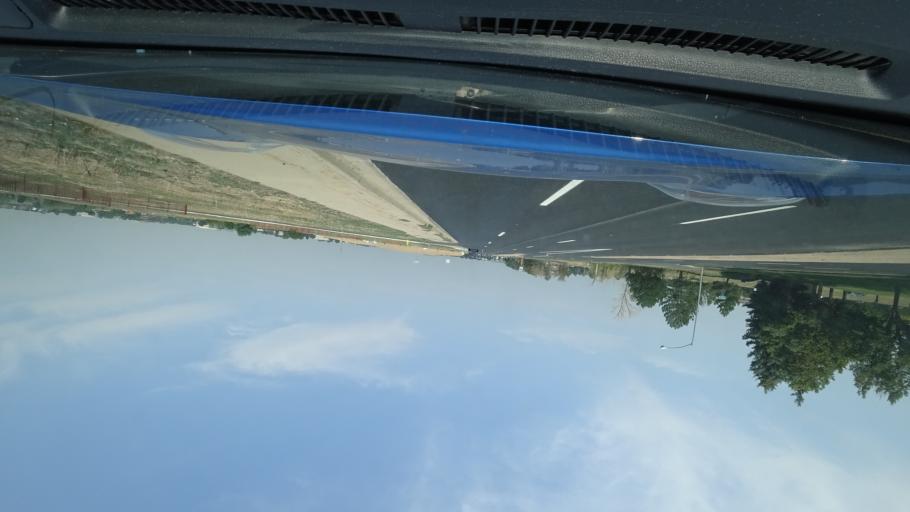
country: US
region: Colorado
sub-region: Adams County
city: Aurora
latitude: 39.7063
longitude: -104.7856
